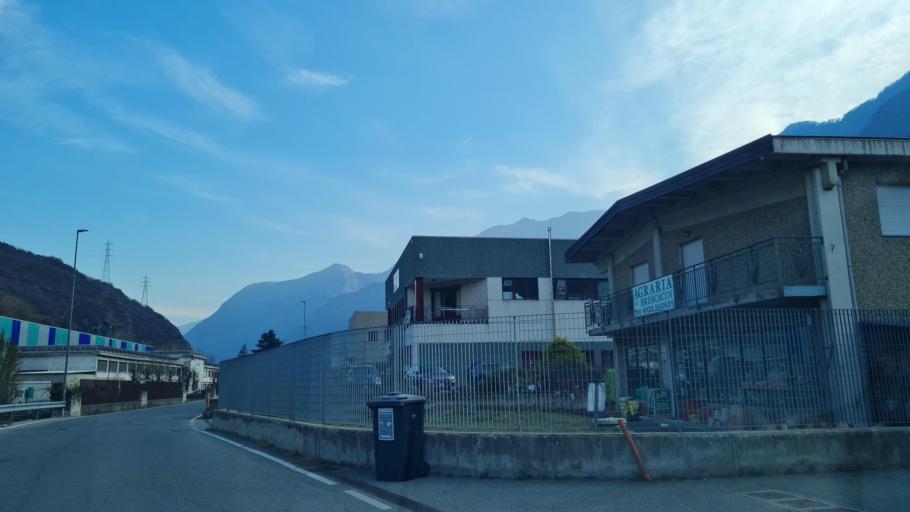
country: IT
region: Aosta Valley
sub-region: Valle d'Aosta
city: Champdepraz
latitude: 45.6863
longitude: 7.6699
